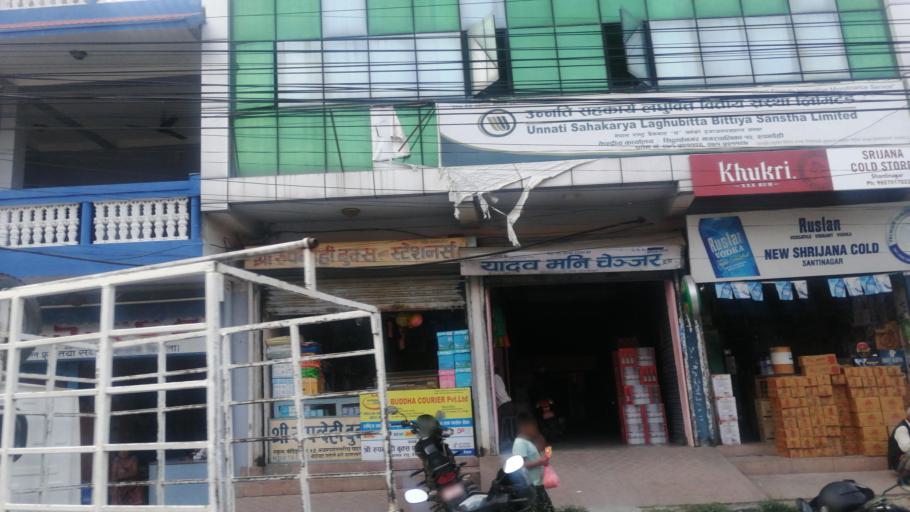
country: NP
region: Western Region
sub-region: Lumbini Zone
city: Bhairahawa
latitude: 27.5059
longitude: 83.4575
